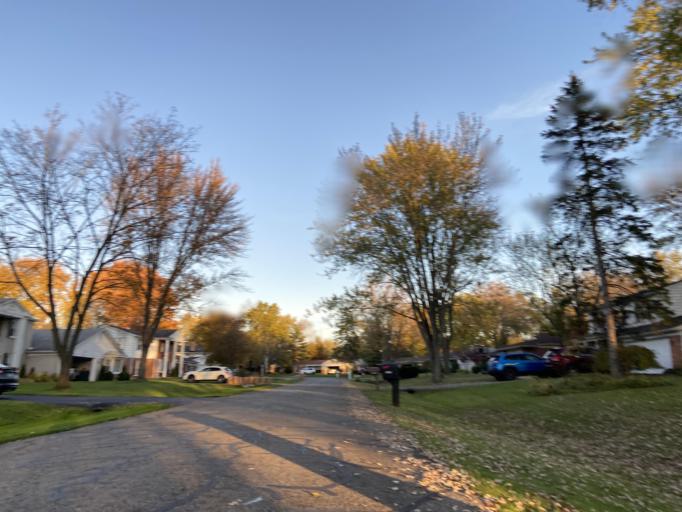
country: US
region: Michigan
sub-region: Oakland County
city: Farmington Hills
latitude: 42.5027
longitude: -83.3681
